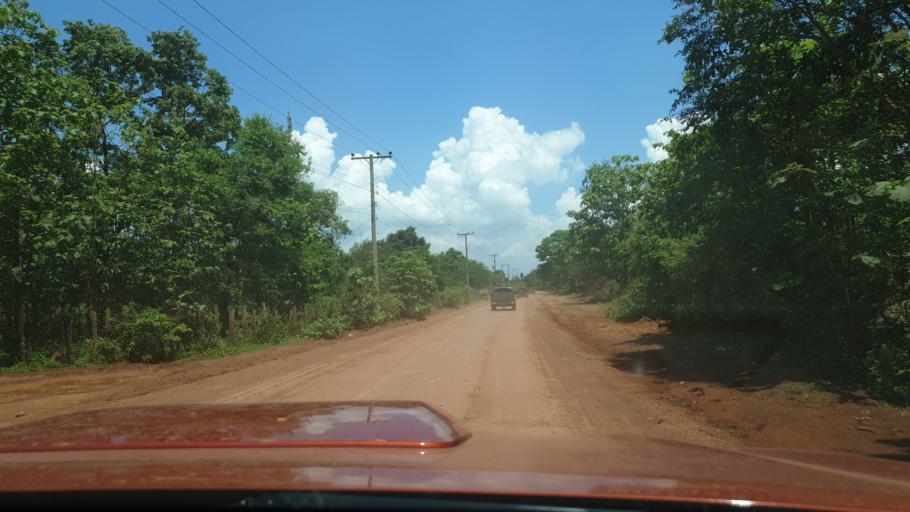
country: LA
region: Champasak
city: Champasak
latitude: 14.7859
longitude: 105.9792
